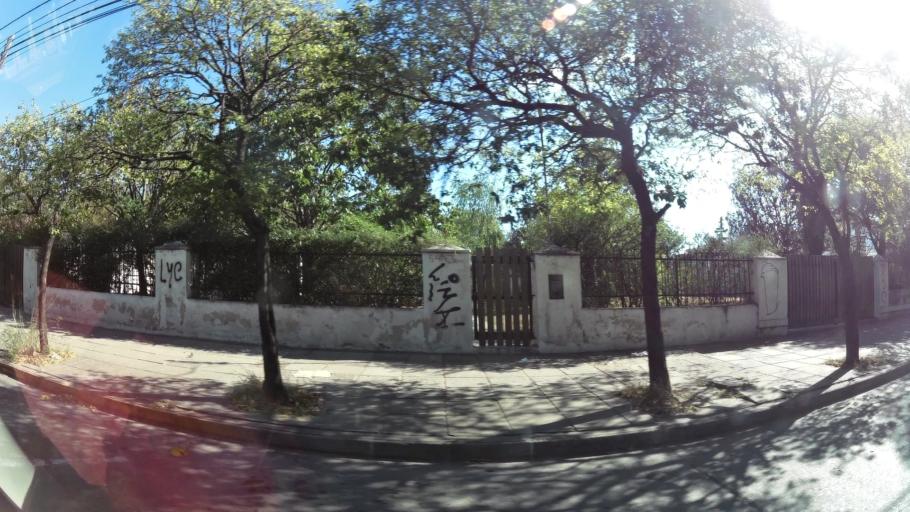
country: AR
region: Cordoba
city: Villa Allende
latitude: -31.3532
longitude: -64.2457
